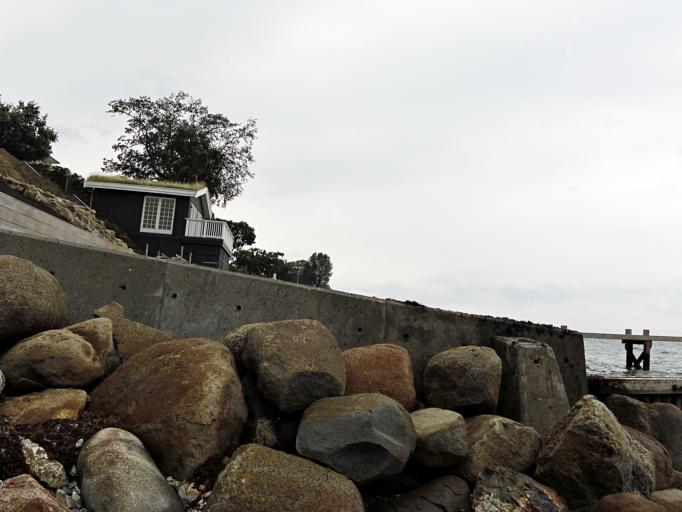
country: DK
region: Capital Region
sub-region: Rudersdal Kommune
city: Trorod
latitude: 55.8603
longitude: 12.5639
